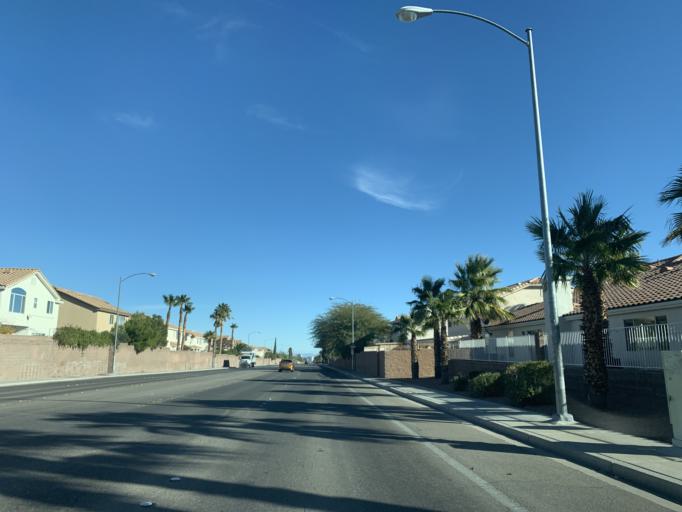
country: US
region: Nevada
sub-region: Clark County
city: Summerlin South
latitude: 36.1225
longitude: -115.3100
